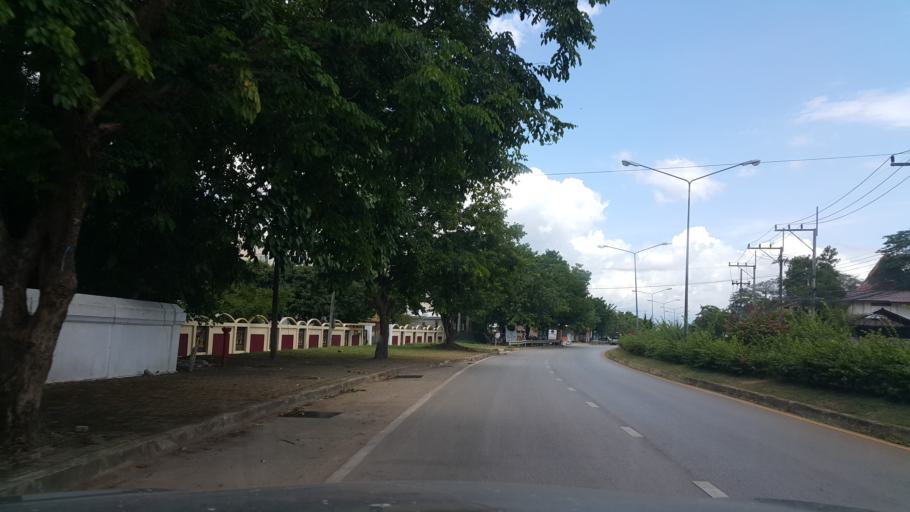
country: TH
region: Phayao
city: Phayao
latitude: 19.1779
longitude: 99.8888
